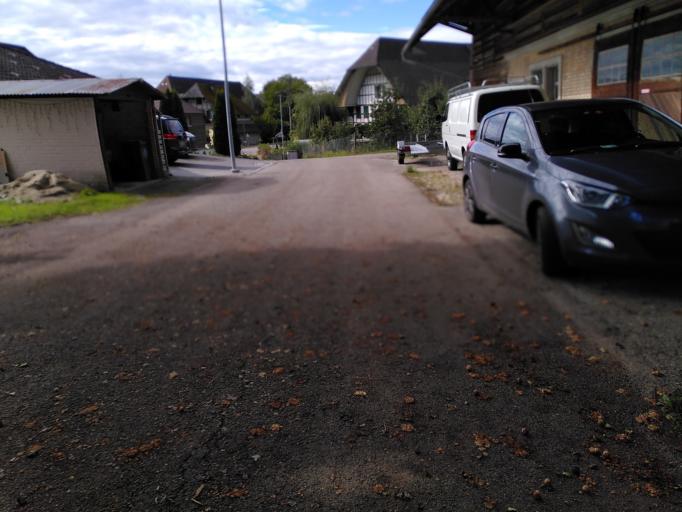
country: CH
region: Bern
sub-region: Emmental District
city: Koppigen
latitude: 47.1170
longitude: 7.6186
